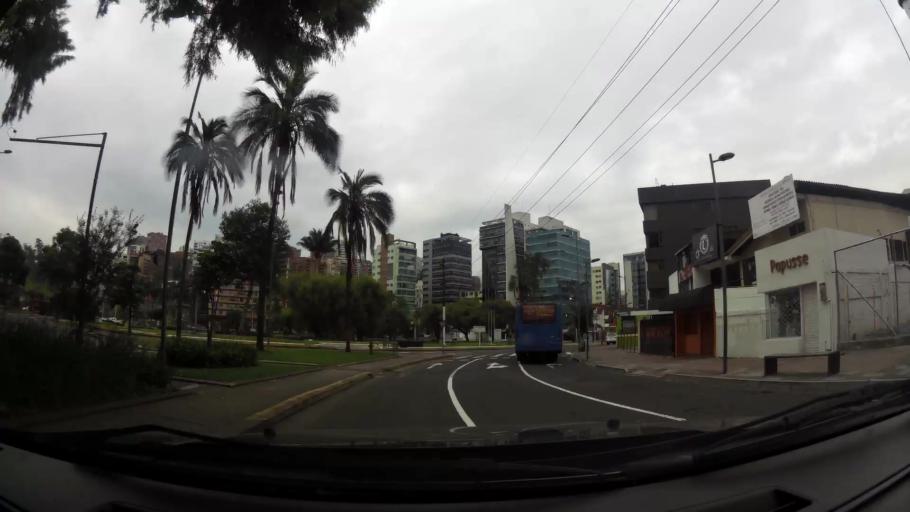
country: EC
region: Pichincha
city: Quito
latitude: -0.1902
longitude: -78.4819
